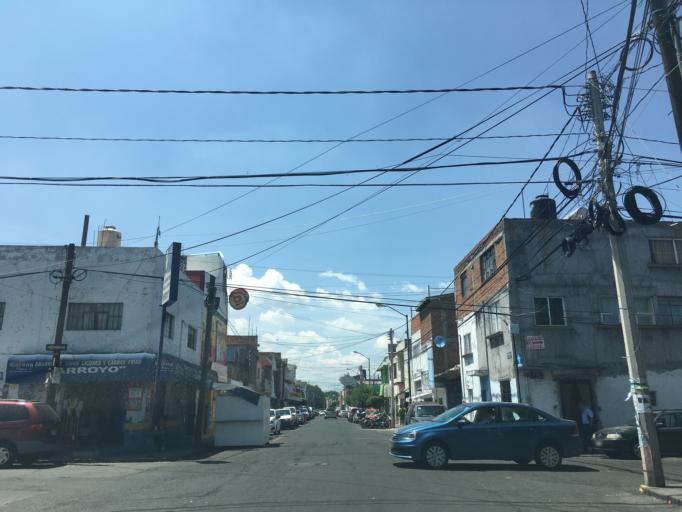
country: MX
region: Michoacan
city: Morelia
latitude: 19.6907
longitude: -101.1864
